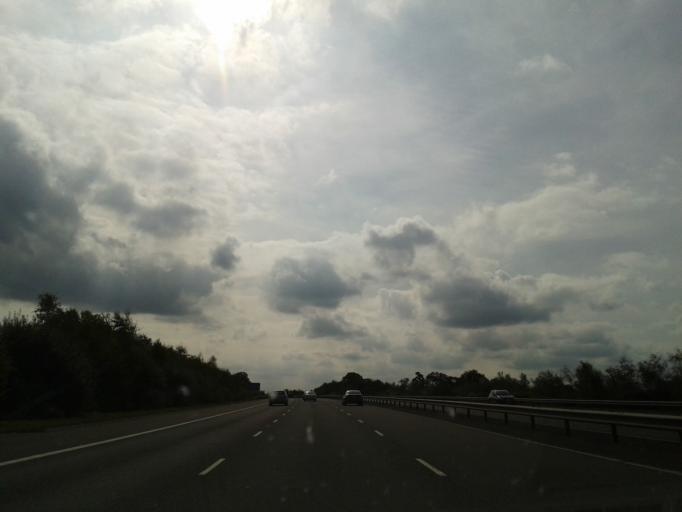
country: GB
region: England
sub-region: City and Borough of Birmingham
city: Sutton Coldfield
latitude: 52.6017
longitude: -1.7968
